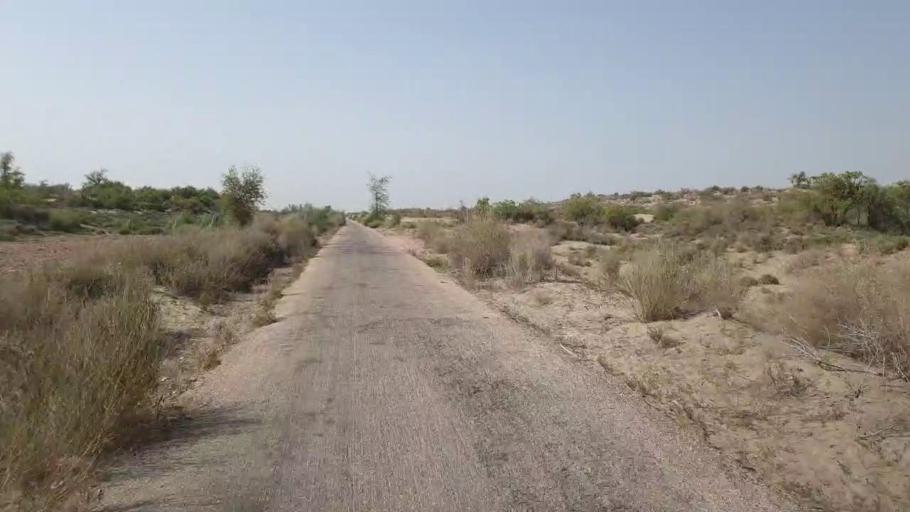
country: PK
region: Sindh
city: Jam Sahib
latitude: 26.5689
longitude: 68.9224
